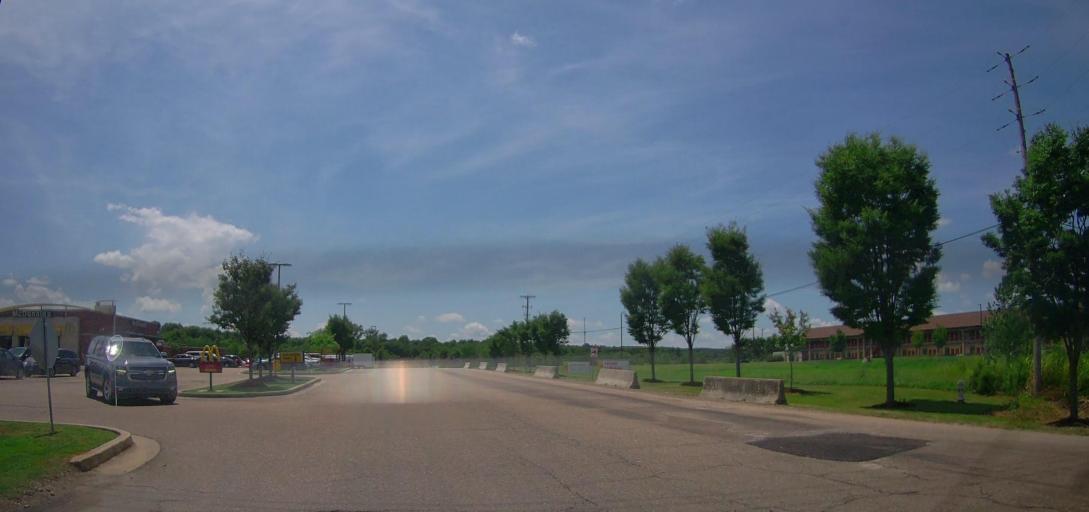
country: US
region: Mississippi
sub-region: Lee County
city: Tupelo
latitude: 34.3170
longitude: -88.7907
